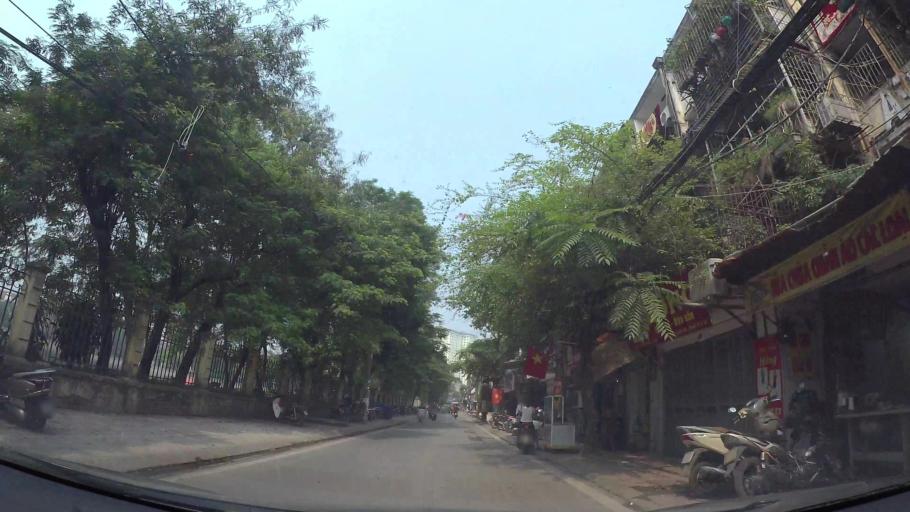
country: VN
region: Ha Noi
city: Dong Da
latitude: 21.0206
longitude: 105.8139
